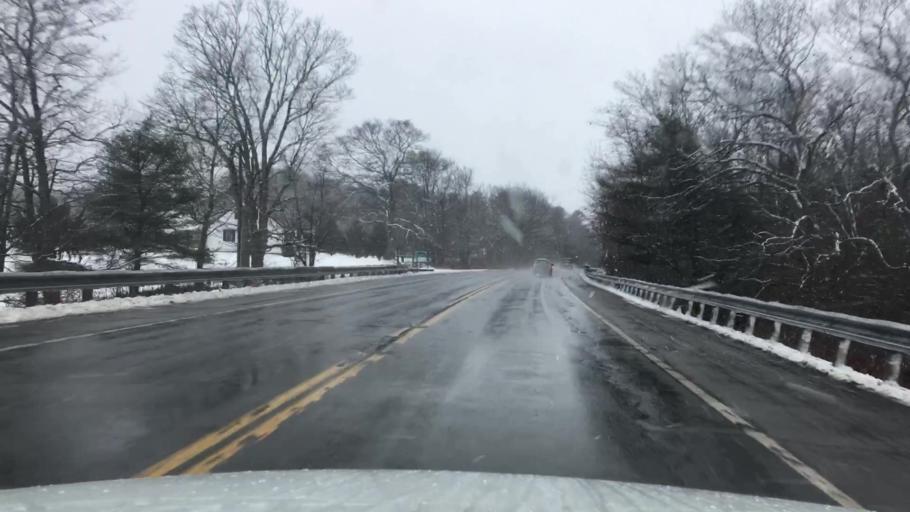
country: US
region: Maine
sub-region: Knox County
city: Warren
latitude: 44.1315
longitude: -69.2270
